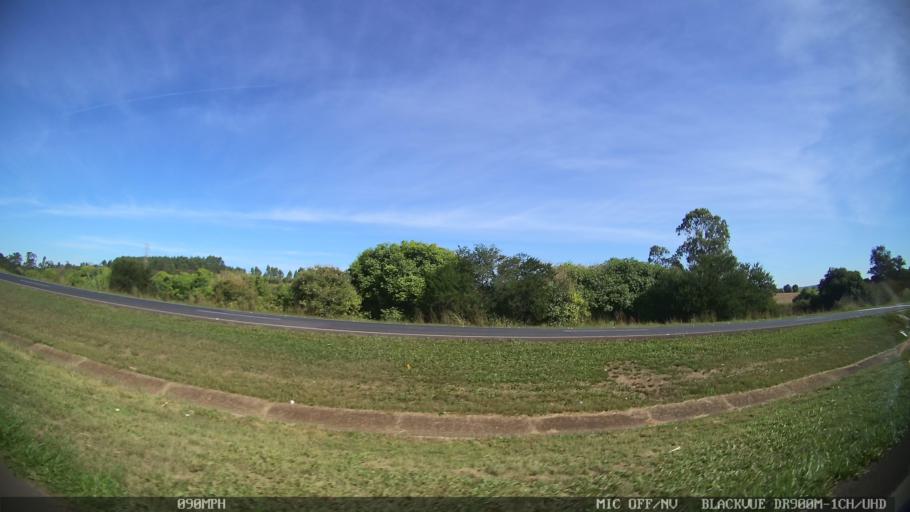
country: BR
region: Sao Paulo
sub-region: Pirassununga
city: Pirassununga
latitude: -22.0599
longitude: -47.4267
